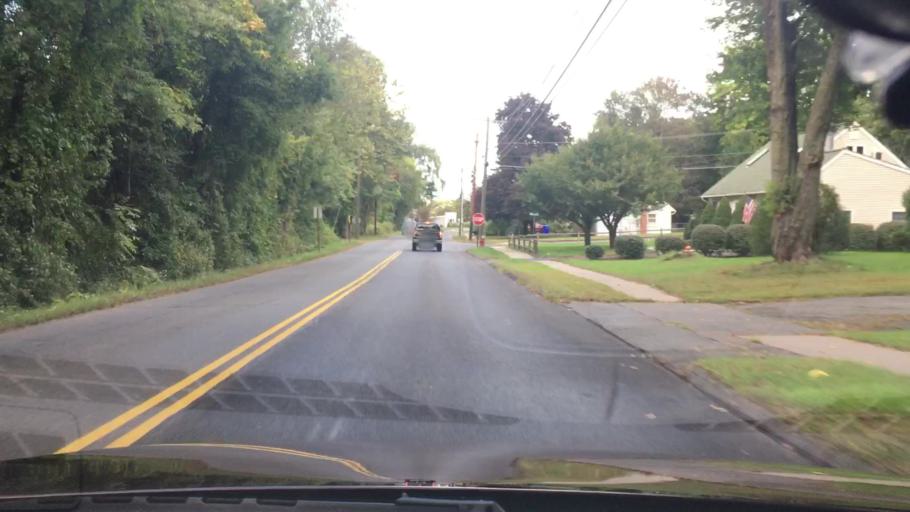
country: US
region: Connecticut
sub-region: Hartford County
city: Hazardville
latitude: 41.9975
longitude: -72.5148
